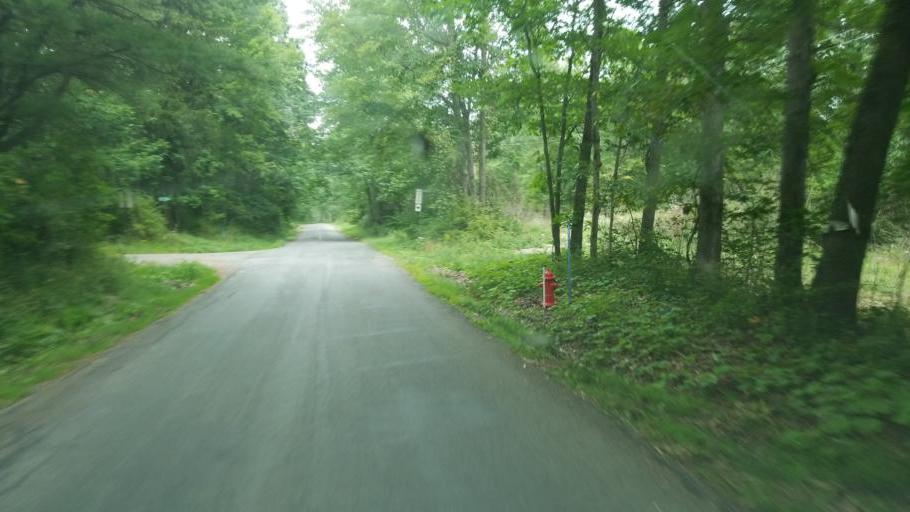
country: US
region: Pennsylvania
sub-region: Clarion County
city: Marianne
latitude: 41.2175
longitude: -79.4186
